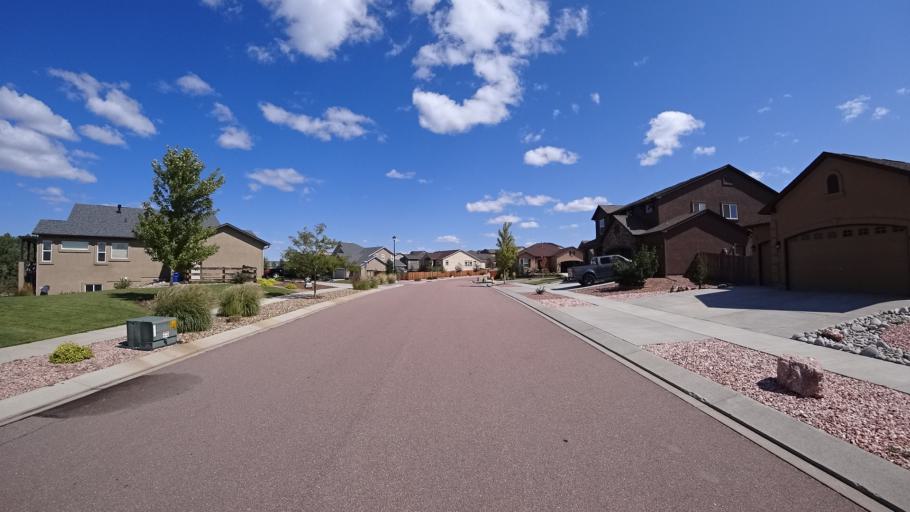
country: US
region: Colorado
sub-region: El Paso County
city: Cimarron Hills
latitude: 38.9316
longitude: -104.6869
